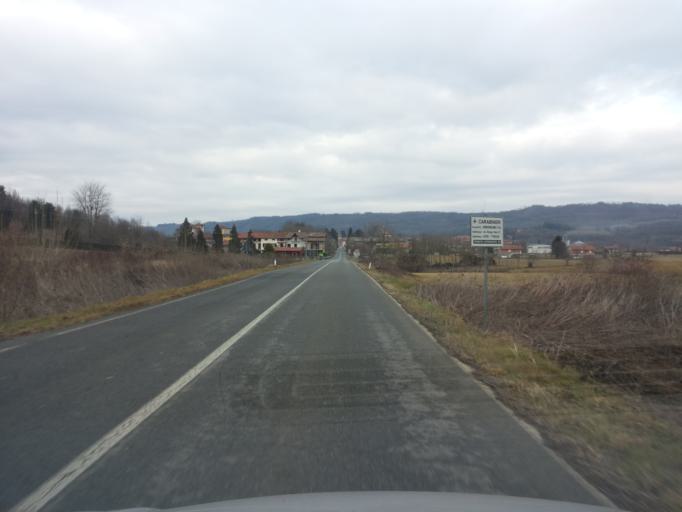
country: IT
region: Piedmont
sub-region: Provincia di Torino
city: Borgomasino
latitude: 45.3515
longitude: 7.9907
